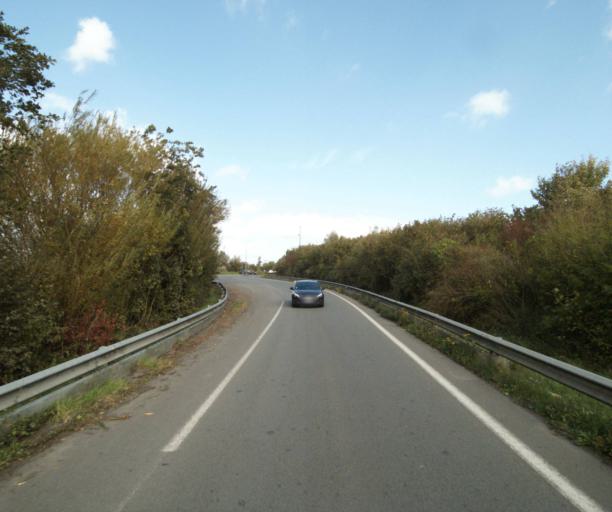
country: FR
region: Nord-Pas-de-Calais
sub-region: Departement du Nord
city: Hallennes-lez-Haubourdin
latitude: 50.6102
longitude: 2.9517
